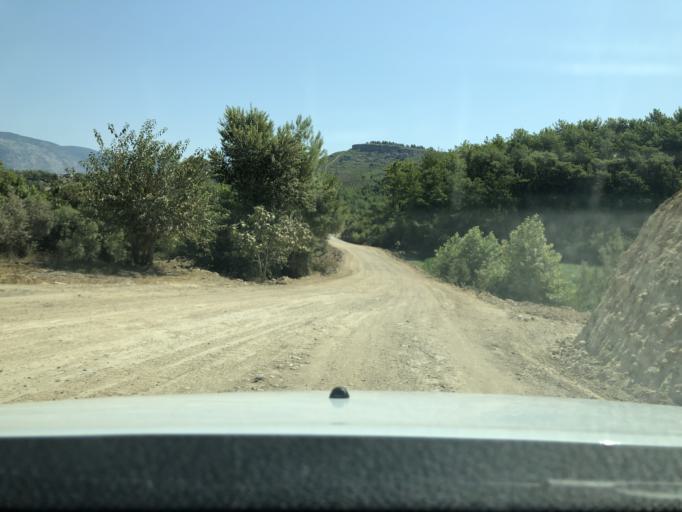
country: TR
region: Antalya
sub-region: Manavgat
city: Manavgat
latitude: 36.8258
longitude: 31.5091
